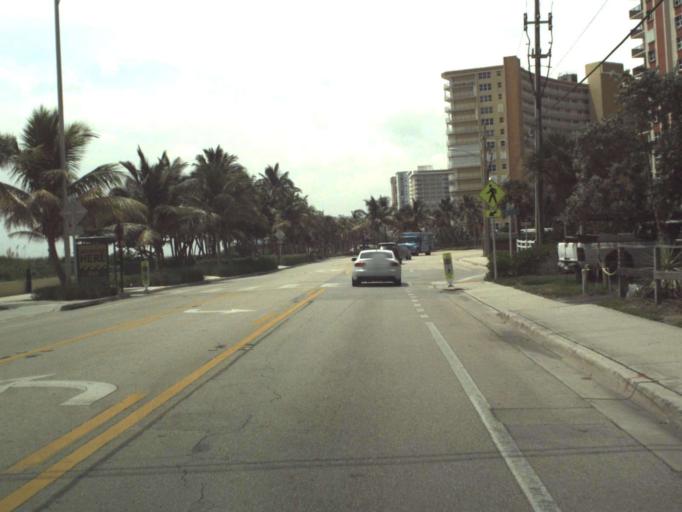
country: US
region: Florida
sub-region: Broward County
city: Terra Mar
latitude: 26.2400
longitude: -80.0884
